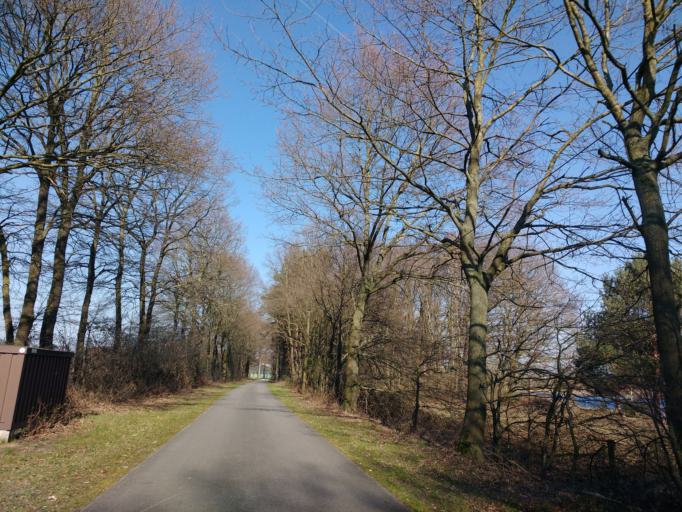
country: DE
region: North Rhine-Westphalia
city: Geseke
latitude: 51.7113
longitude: 8.5061
